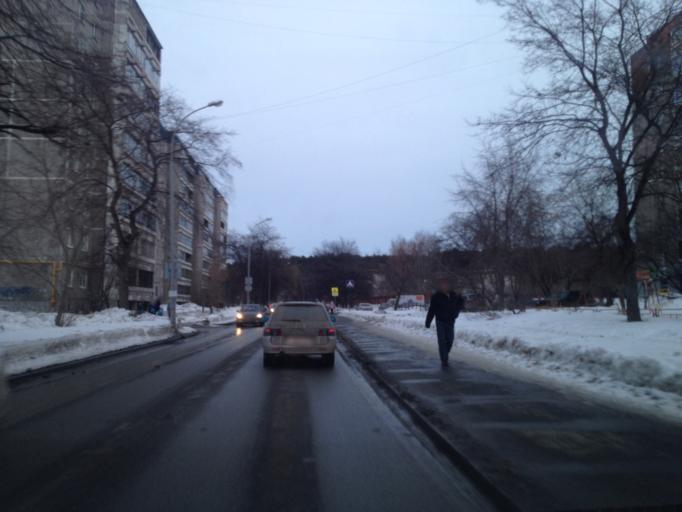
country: RU
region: Sverdlovsk
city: Sovkhoznyy
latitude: 56.7967
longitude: 60.5871
